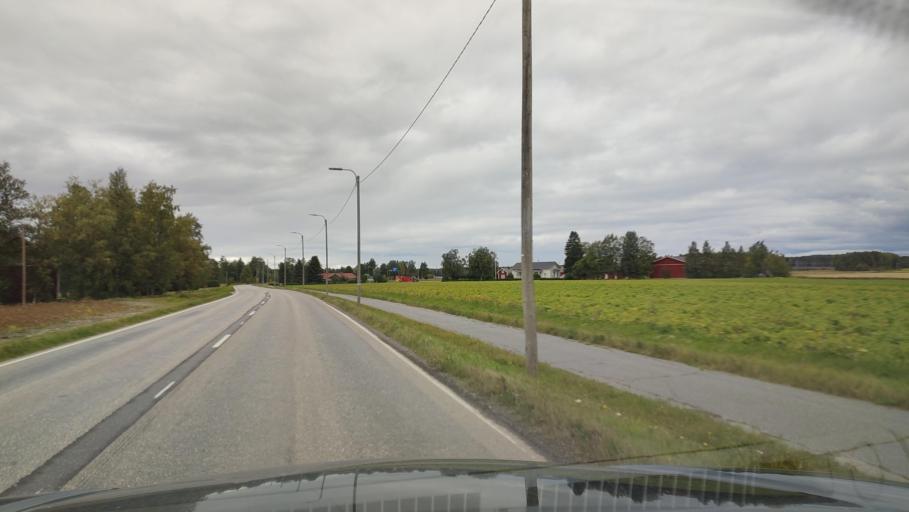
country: FI
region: Ostrobothnia
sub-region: Sydosterbotten
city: Kristinestad
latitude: 62.2570
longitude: 21.4972
